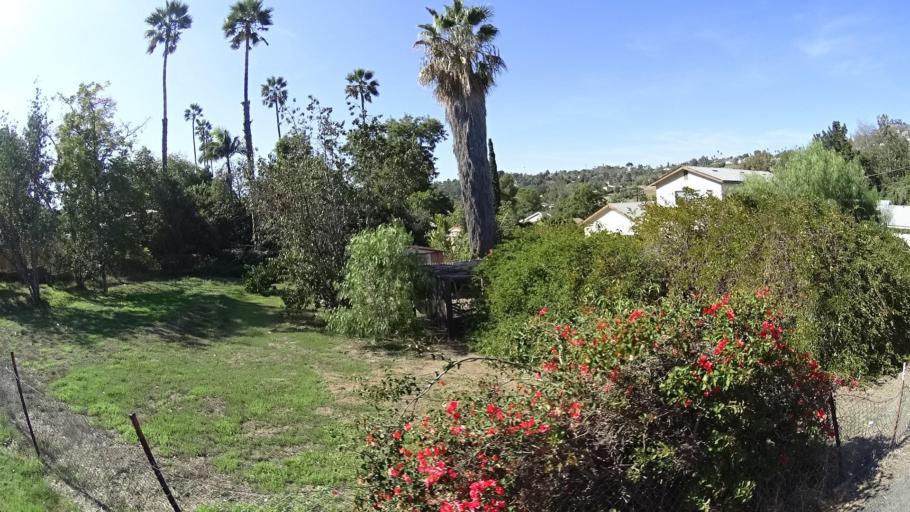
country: US
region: California
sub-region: San Diego County
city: Spring Valley
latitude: 32.7506
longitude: -116.9819
